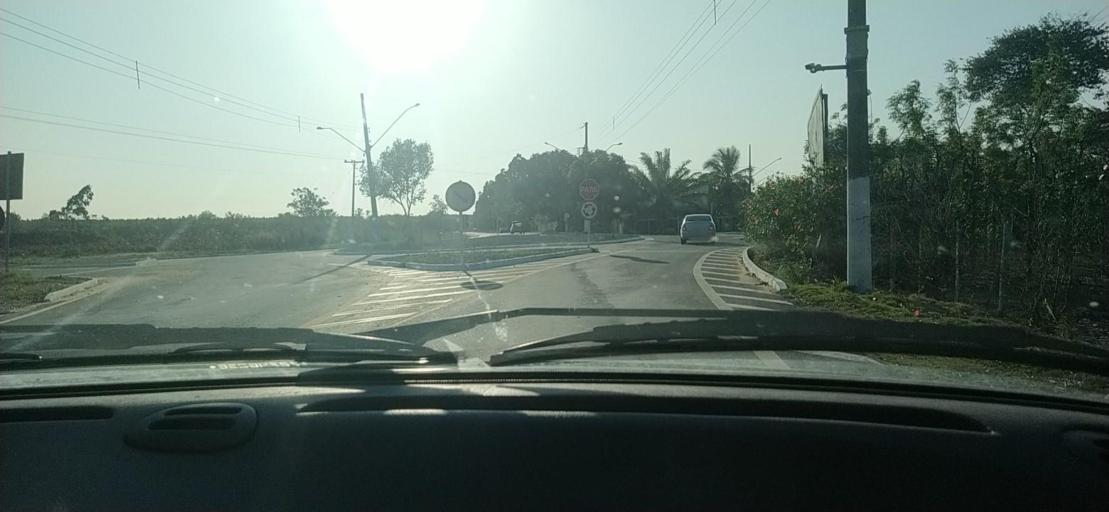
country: BR
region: Espirito Santo
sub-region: Conceicao Da Barra
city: Conceicao da Barra
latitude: -18.5658
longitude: -39.7634
